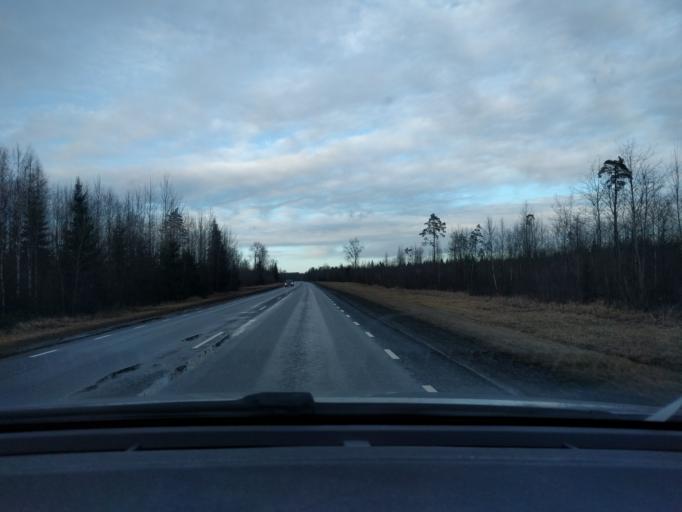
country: EE
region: Viljandimaa
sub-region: Vohma linn
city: Vohma
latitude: 58.6125
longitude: 25.5714
